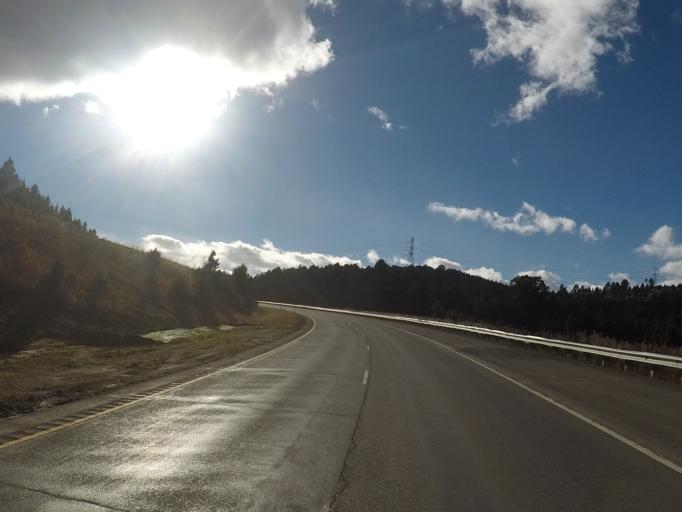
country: US
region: Montana
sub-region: Jefferson County
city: Boulder
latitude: 46.3289
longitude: -112.0619
